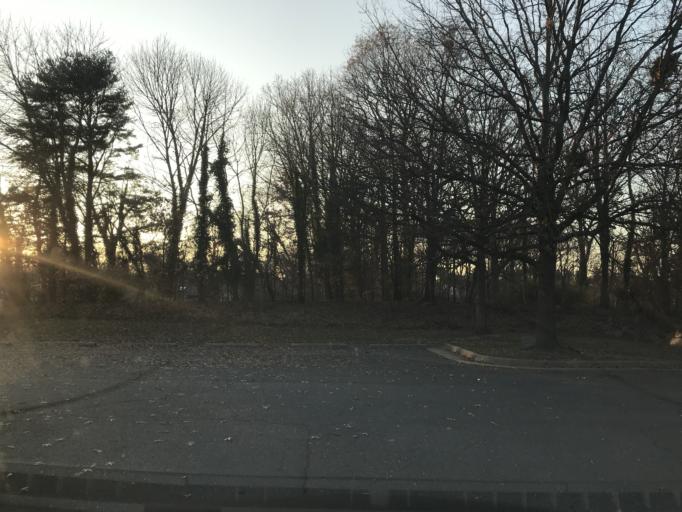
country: US
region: Virginia
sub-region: Fairfax County
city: Franconia
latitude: 38.7883
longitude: -77.1634
